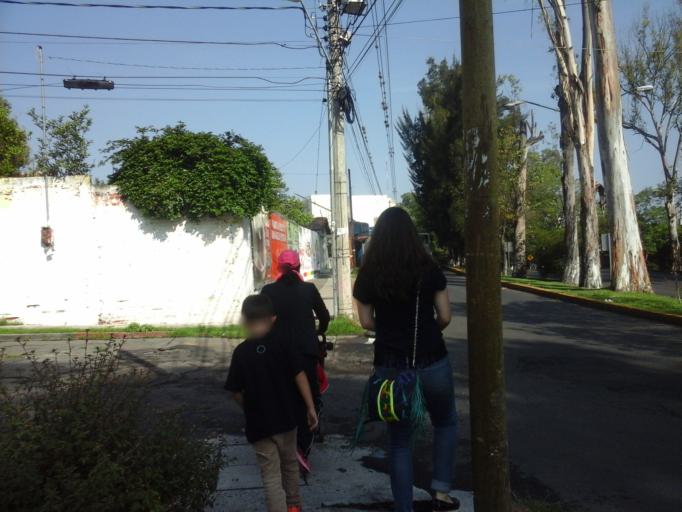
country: MX
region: Michoacan
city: Morelia
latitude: 19.6810
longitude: -101.1872
